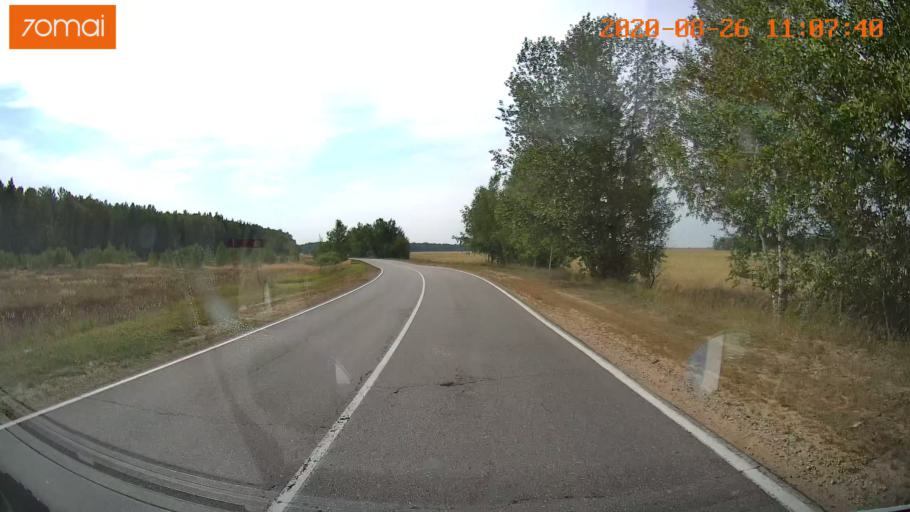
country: RU
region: Rjazan
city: Izhevskoye
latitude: 54.5159
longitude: 41.1205
